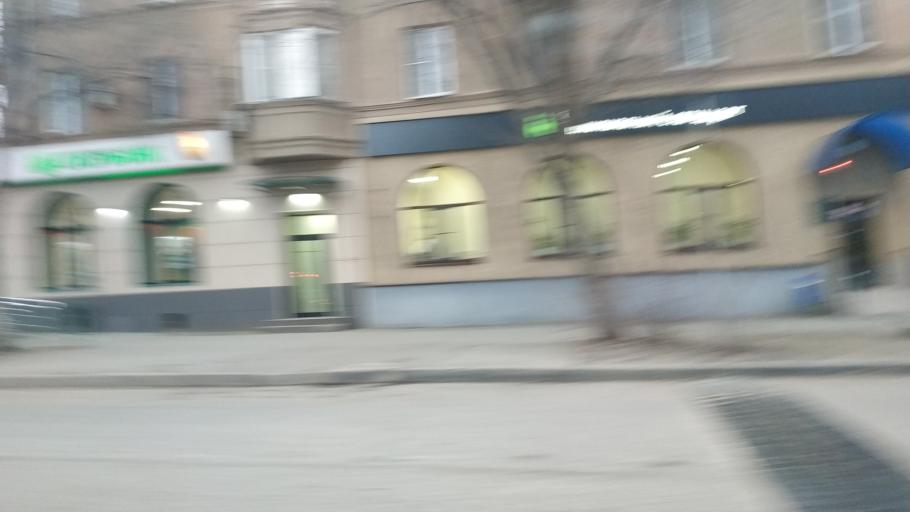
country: RU
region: Astrakhan
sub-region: Gorod Astrakhan'
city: Astrakhan'
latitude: 46.3351
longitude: 48.0183
